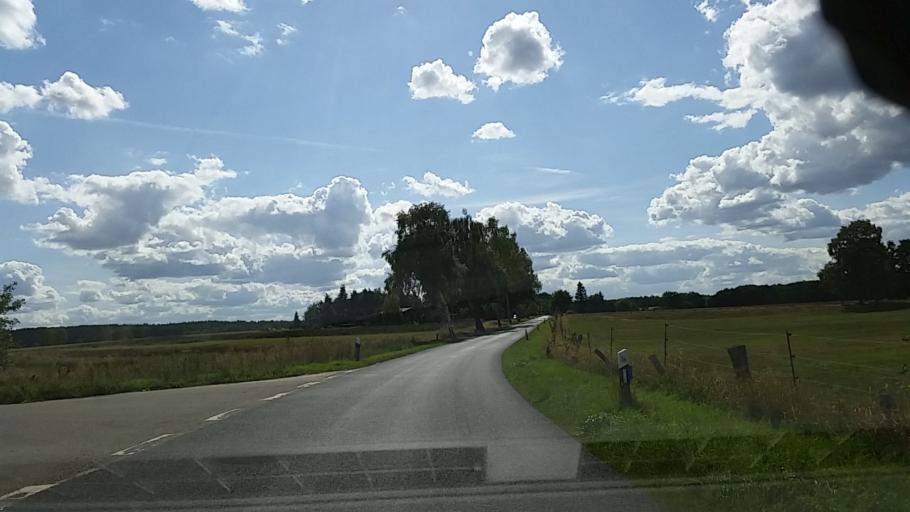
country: DE
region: Lower Saxony
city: Bienenbuttel
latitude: 53.1288
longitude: 10.4293
